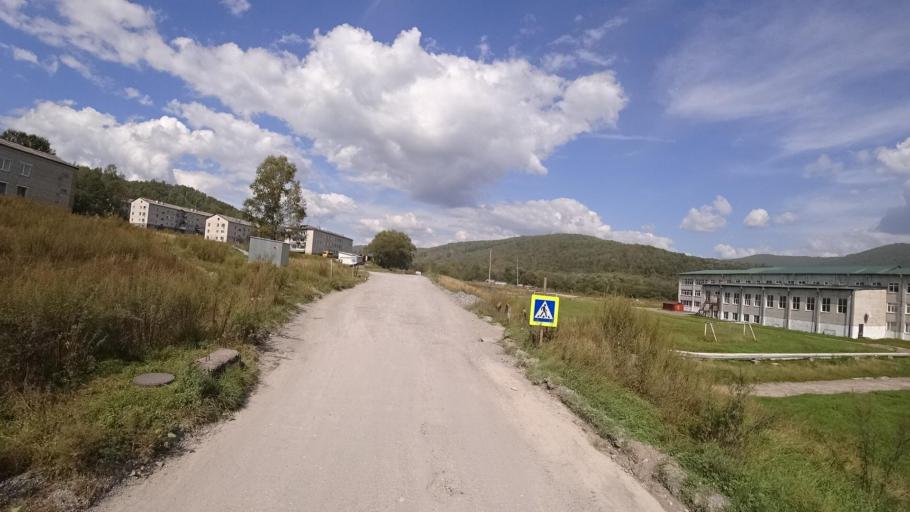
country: RU
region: Jewish Autonomous Oblast
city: Londoko
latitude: 49.0264
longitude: 131.9246
